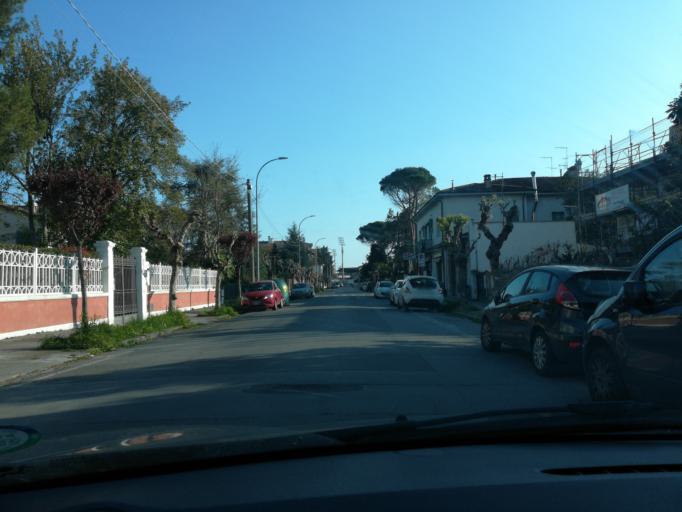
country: IT
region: Tuscany
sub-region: Province of Pisa
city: Pisa
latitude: 43.7303
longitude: 10.4001
